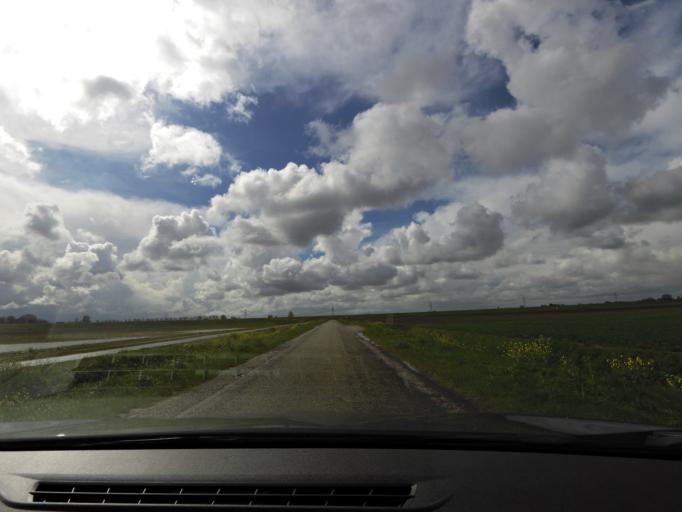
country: NL
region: South Holland
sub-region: Gemeente Oud-Beijerland
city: Oud-Beijerland
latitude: 51.8228
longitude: 4.3689
